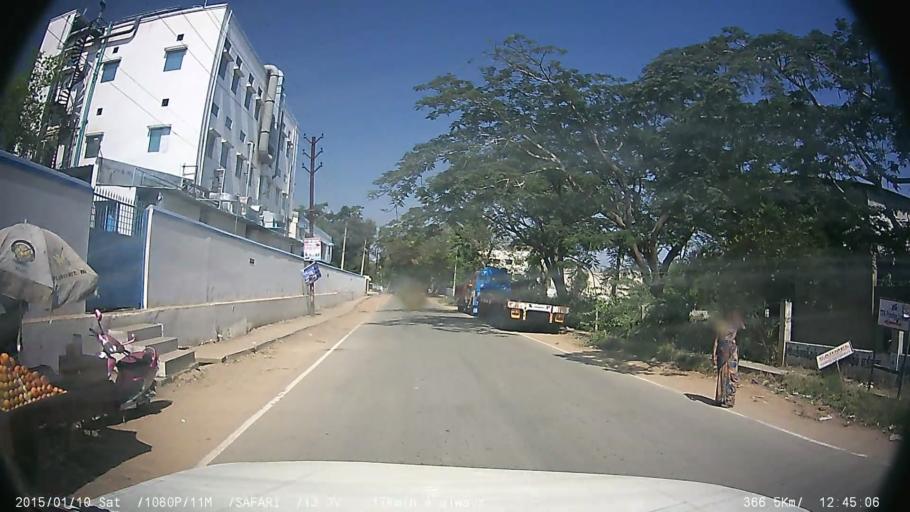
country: IN
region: Tamil Nadu
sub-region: Krishnagiri
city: Hosur
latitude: 12.7640
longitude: 77.7957
